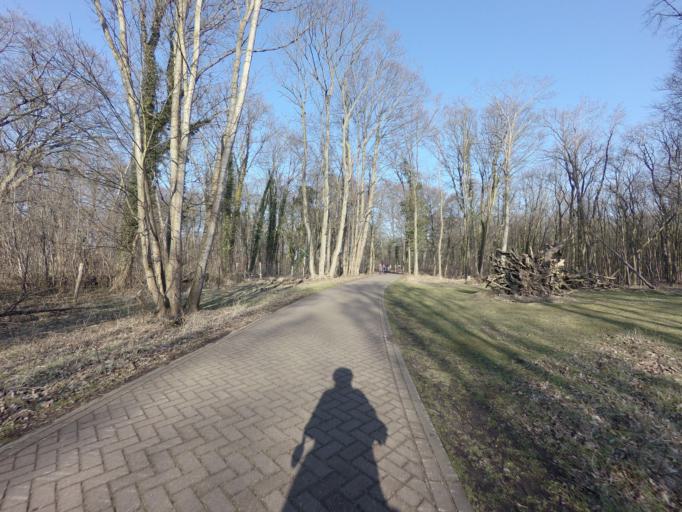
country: NL
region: North Holland
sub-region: Gemeente Velsen
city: Velsen-Zuid
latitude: 52.4529
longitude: 4.6150
